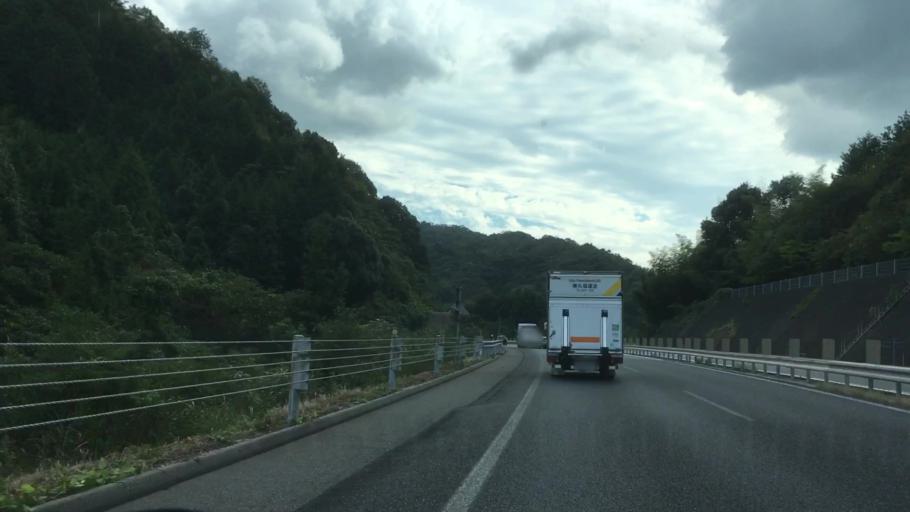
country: JP
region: Yamaguchi
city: Iwakuni
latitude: 34.1261
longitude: 132.1110
